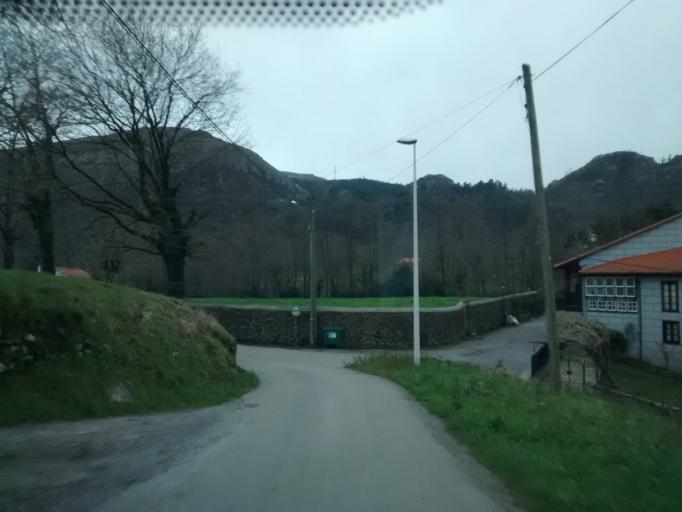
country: ES
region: Cantabria
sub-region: Provincia de Cantabria
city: Entrambasaguas
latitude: 43.3455
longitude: -3.6940
